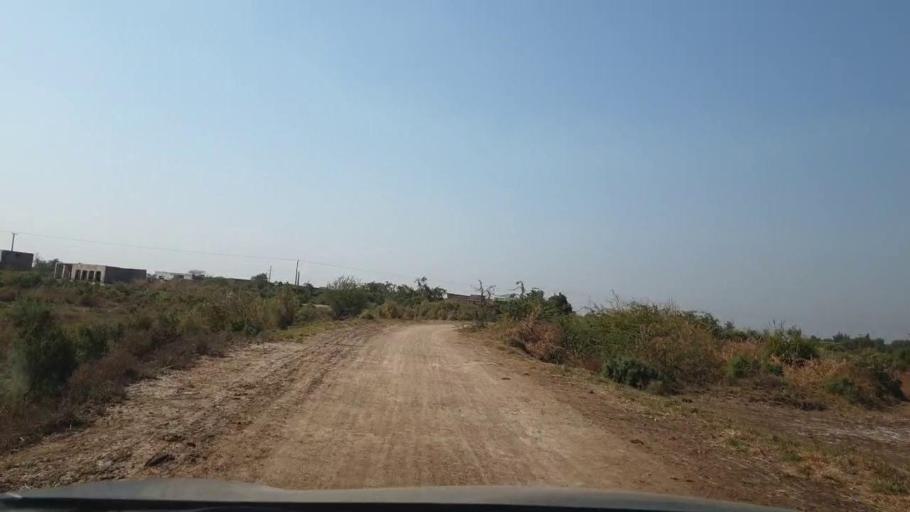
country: PK
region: Sindh
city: Berani
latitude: 25.7128
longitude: 68.8587
